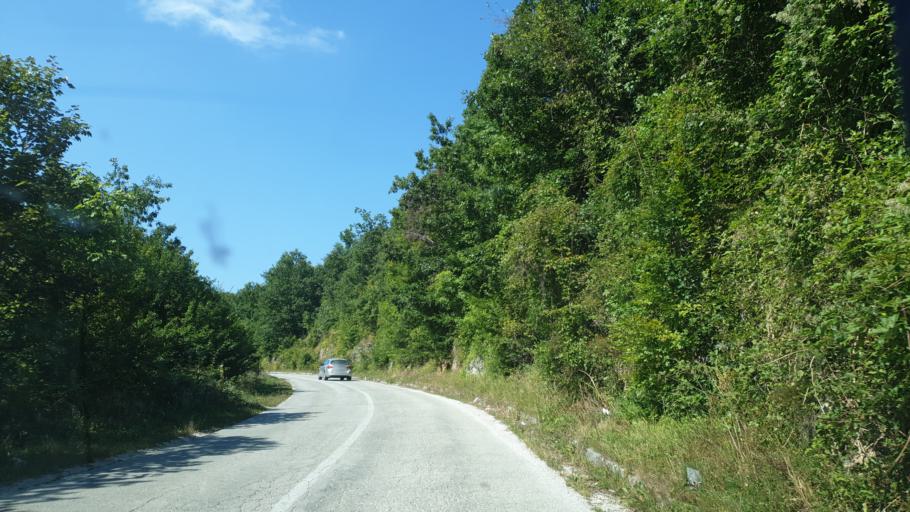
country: RS
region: Central Serbia
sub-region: Zlatiborski Okrug
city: Cajetina
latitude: 43.7121
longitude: 19.8361
